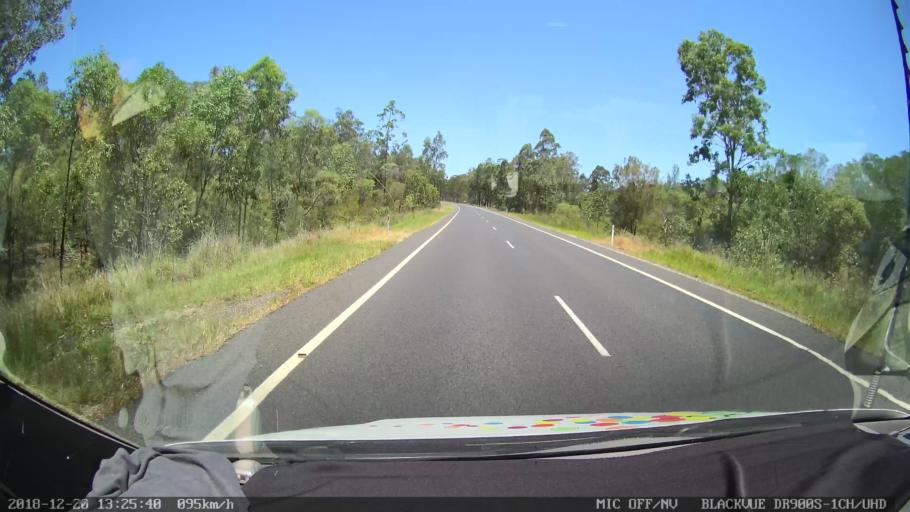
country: AU
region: New South Wales
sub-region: Richmond Valley
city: Casino
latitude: -29.1344
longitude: 152.9959
